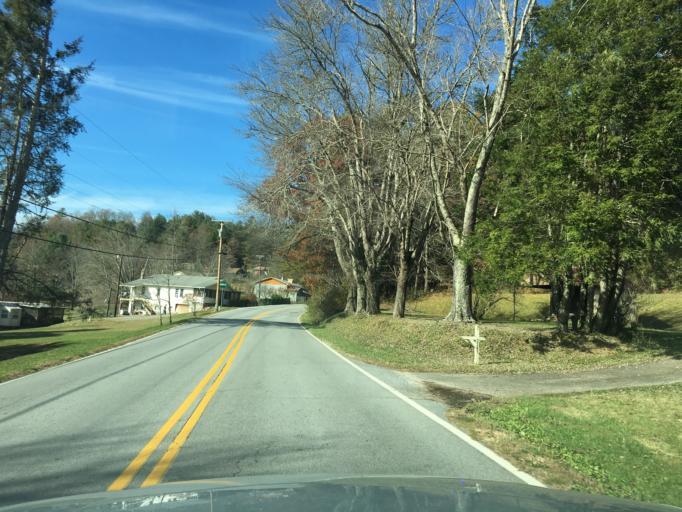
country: US
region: North Carolina
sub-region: Henderson County
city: Etowah
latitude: 35.2428
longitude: -82.6311
